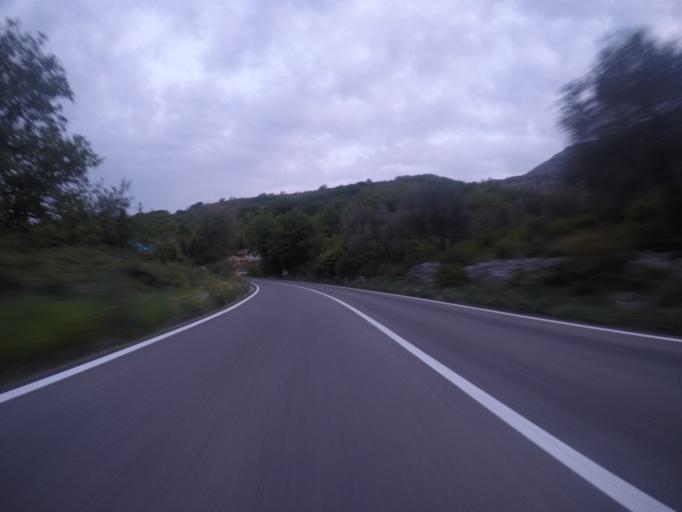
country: ME
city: Petrovac na Moru
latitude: 42.1979
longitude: 18.9779
